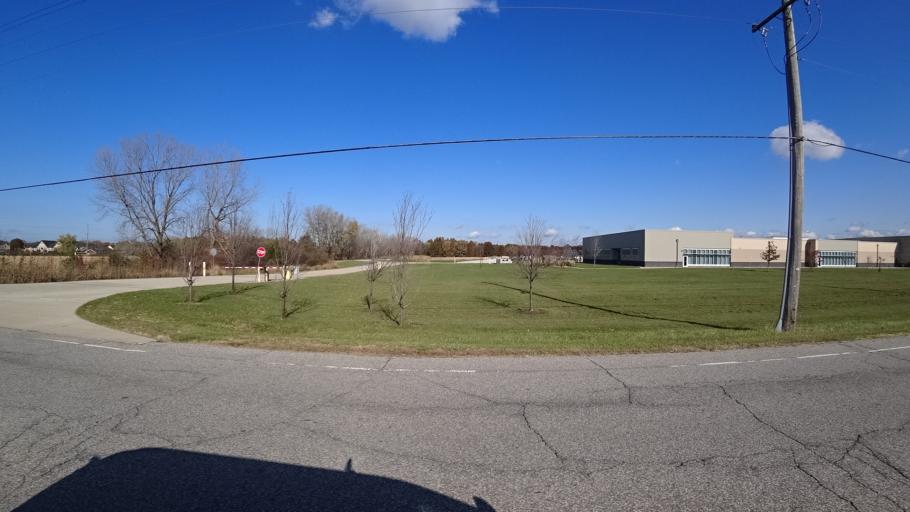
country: US
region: Indiana
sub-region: LaPorte County
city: Trail Creek
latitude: 41.6803
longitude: -86.8729
